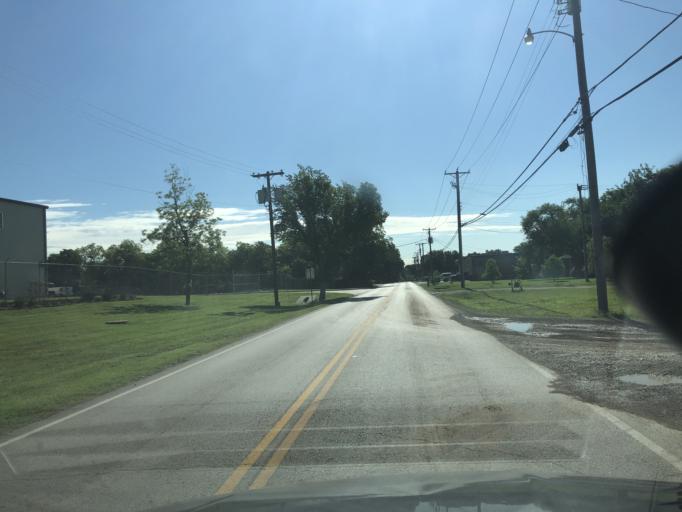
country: US
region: Texas
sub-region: Dallas County
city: Grand Prairie
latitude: 32.8034
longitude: -97.0241
